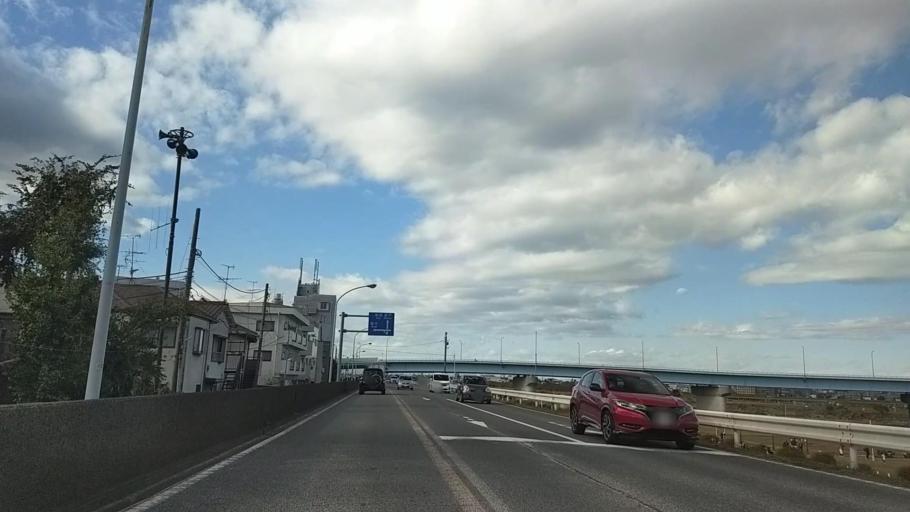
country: JP
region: Tokyo
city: Chofugaoka
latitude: 35.6088
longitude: 139.6217
